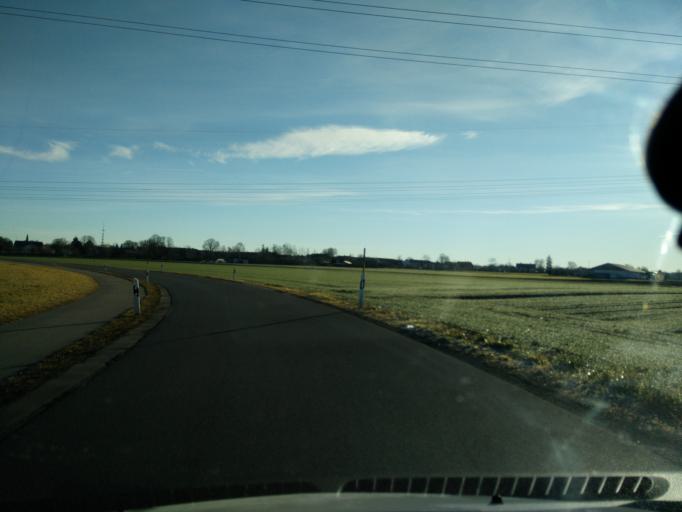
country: DE
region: Bavaria
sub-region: Upper Bavaria
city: Puchheim
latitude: 48.1277
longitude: 11.3419
